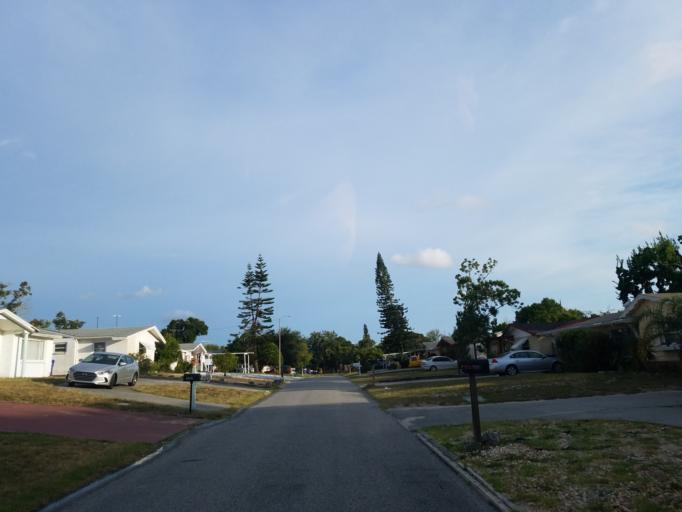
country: US
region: Florida
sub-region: Pasco County
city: Beacon Square
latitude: 28.2079
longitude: -82.7479
